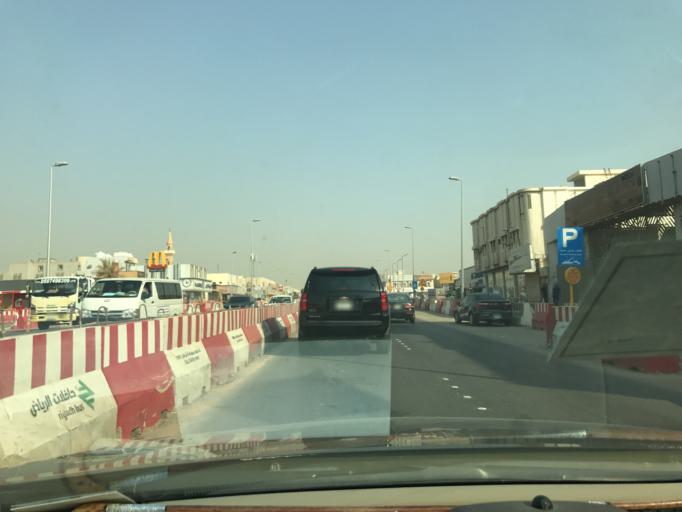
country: SA
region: Ar Riyad
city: Riyadh
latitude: 24.7526
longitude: 46.7705
